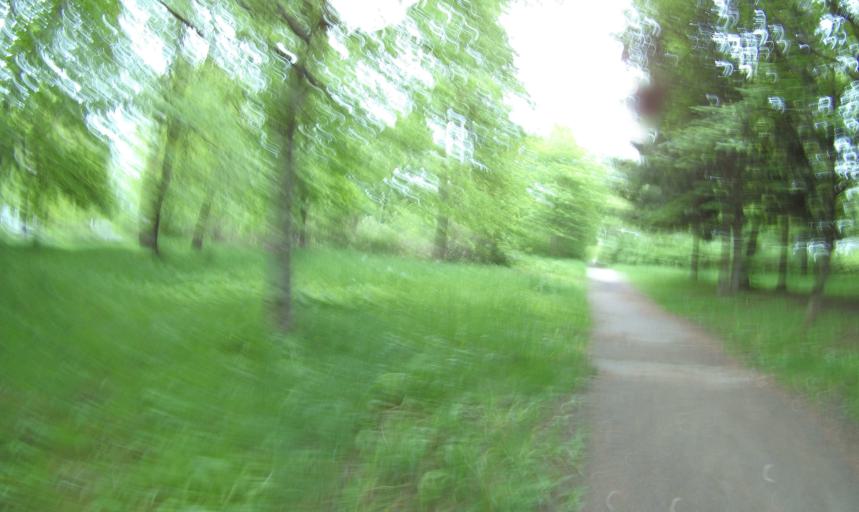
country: RU
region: Moskovskaya
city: Kolomna
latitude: 55.0706
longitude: 38.8042
